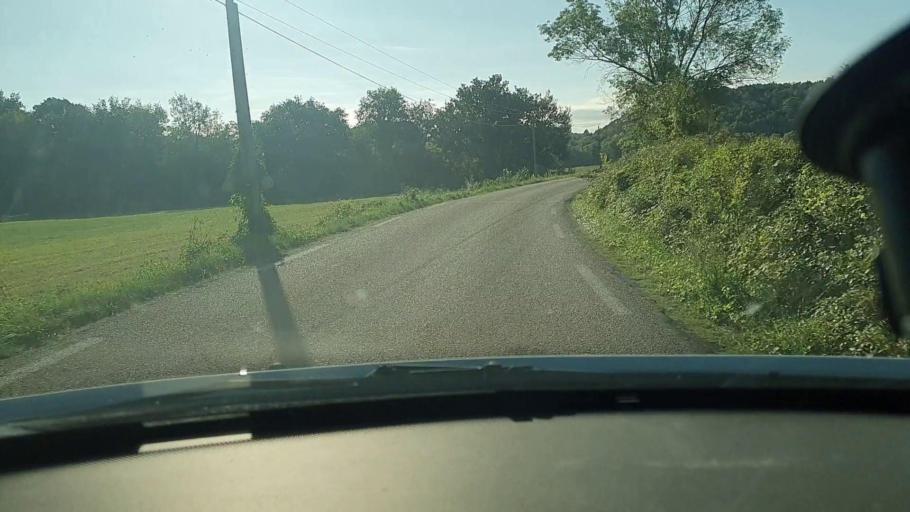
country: FR
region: Languedoc-Roussillon
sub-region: Departement du Gard
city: Goudargues
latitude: 44.2028
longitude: 4.4705
